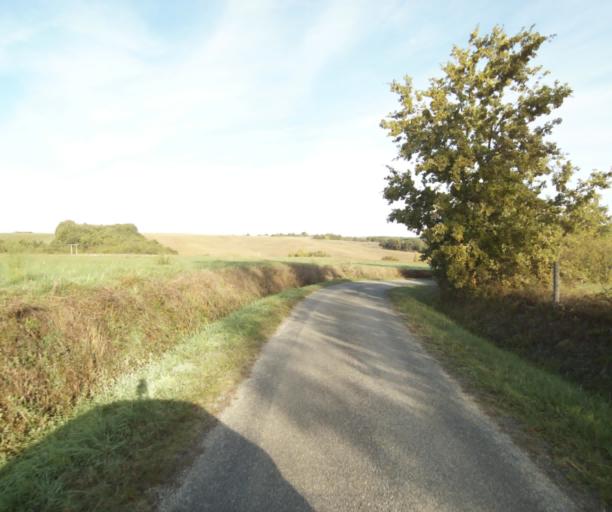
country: FR
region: Midi-Pyrenees
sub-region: Departement de la Haute-Garonne
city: Villemur-sur-Tarn
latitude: 43.9091
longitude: 1.5010
